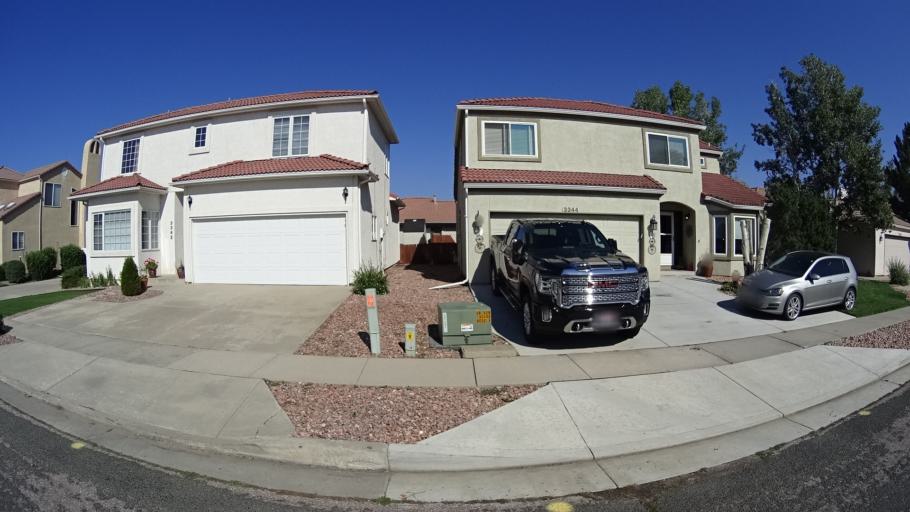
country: US
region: Colorado
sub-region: El Paso County
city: Colorado Springs
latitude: 38.8798
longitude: -104.7919
